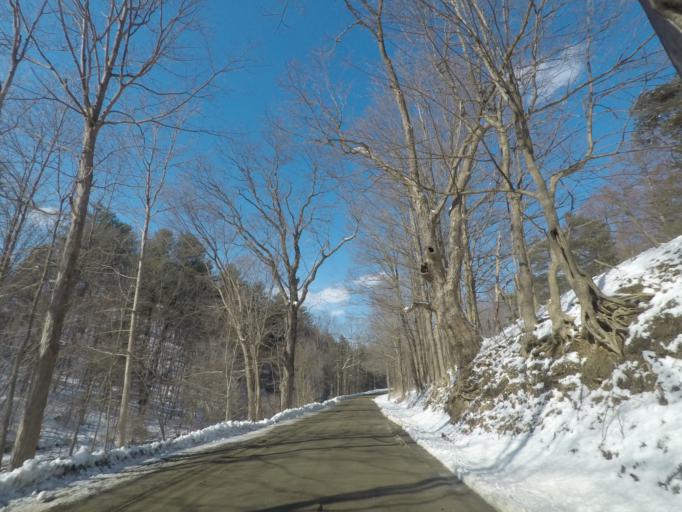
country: US
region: New York
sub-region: Saratoga County
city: Waterford
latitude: 42.8138
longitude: -73.6055
